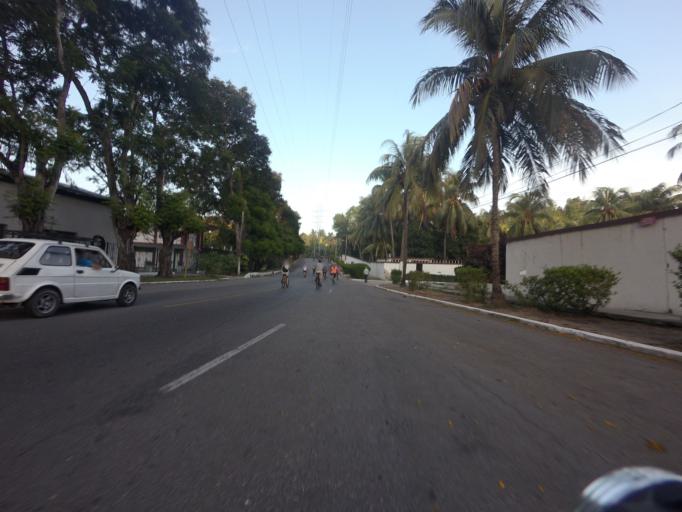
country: CU
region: La Habana
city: Cerro
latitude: 23.1077
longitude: -82.4058
